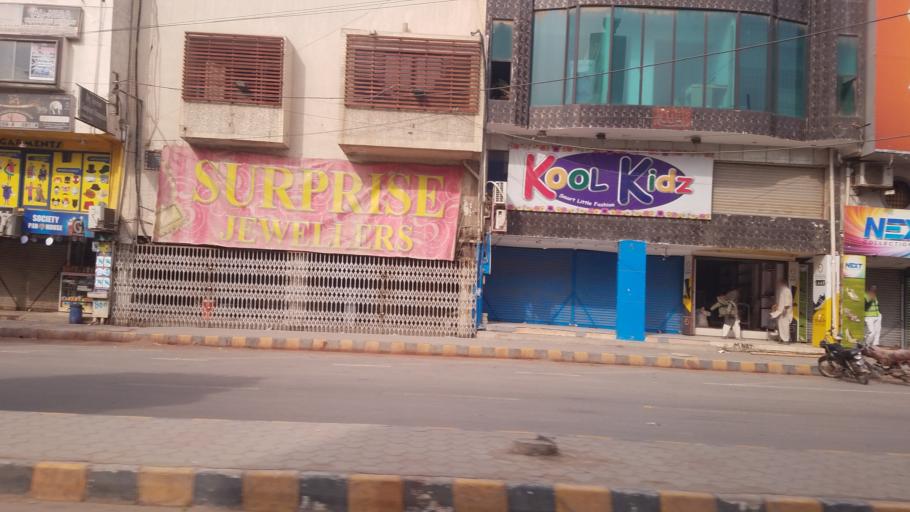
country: PK
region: Sindh
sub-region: Karachi District
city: Karachi
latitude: 24.8717
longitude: 67.0597
